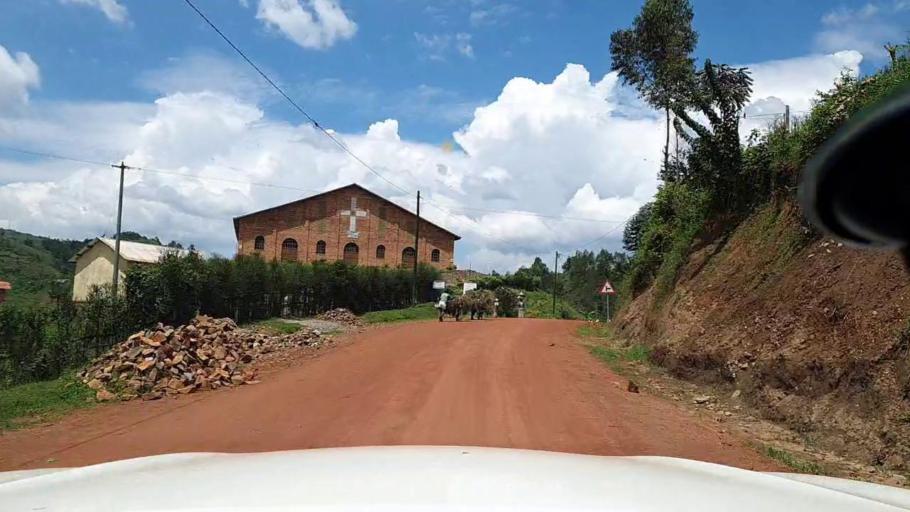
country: RW
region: Northern Province
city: Byumba
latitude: -1.7039
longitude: 29.8373
